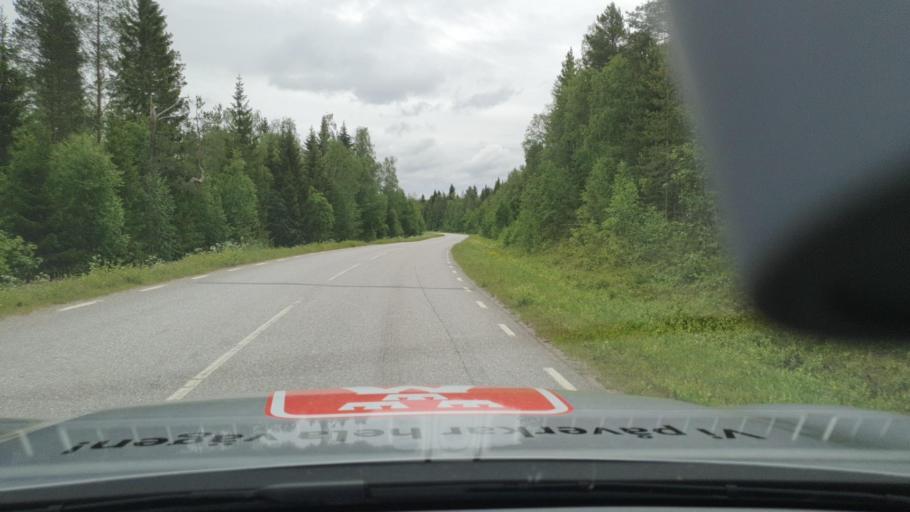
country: SE
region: Norrbotten
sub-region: Lulea Kommun
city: Ranea
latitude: 65.8845
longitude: 22.2005
